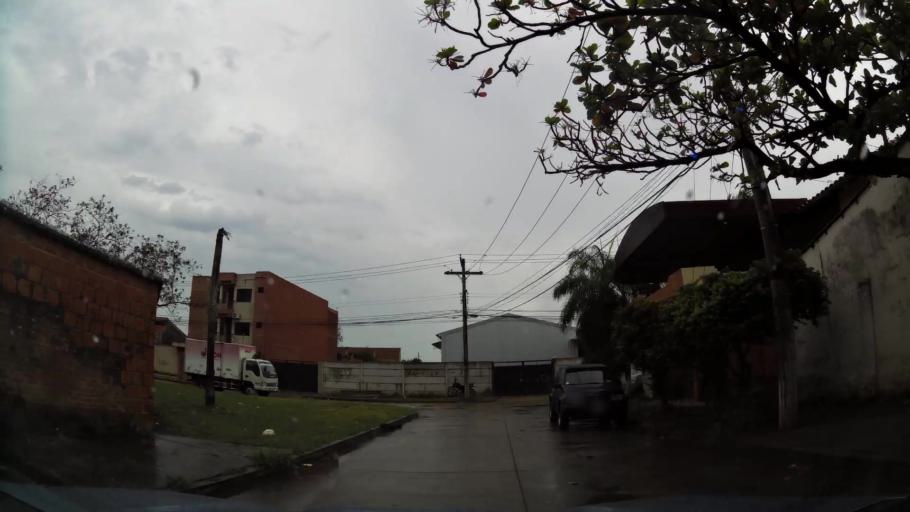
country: BO
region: Santa Cruz
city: Santa Cruz de la Sierra
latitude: -17.7840
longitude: -63.1528
